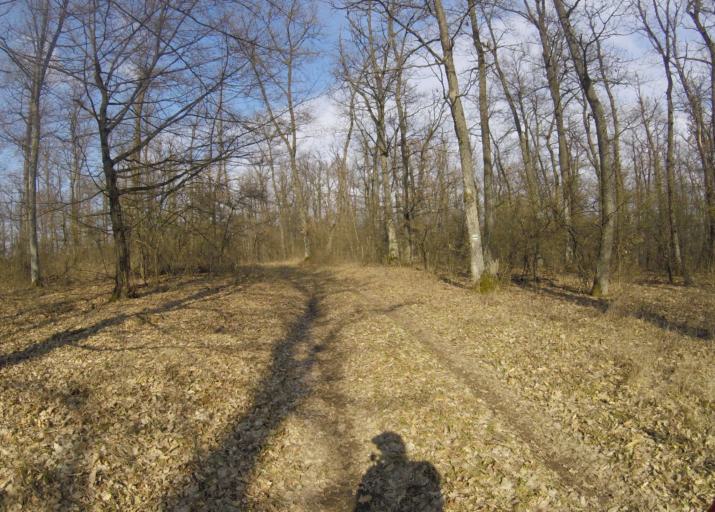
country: HU
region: Heves
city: Belapatfalva
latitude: 47.9986
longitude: 20.3450
